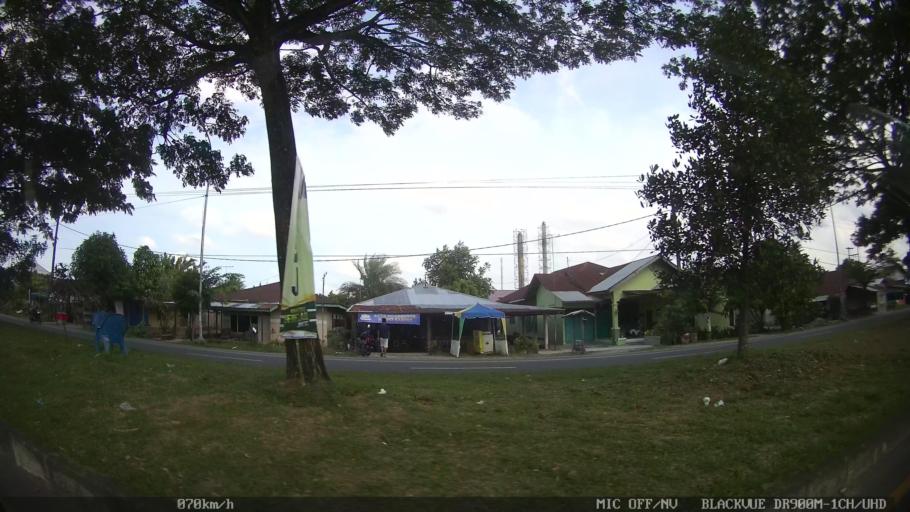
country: ID
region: North Sumatra
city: Percut
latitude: 3.5667
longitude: 98.7949
